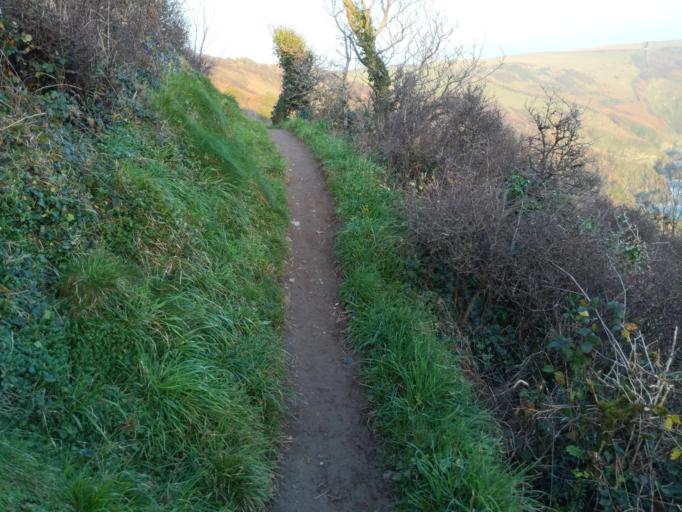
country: GB
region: England
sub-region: Cornwall
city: Fowey
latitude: 50.3276
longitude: -4.6150
